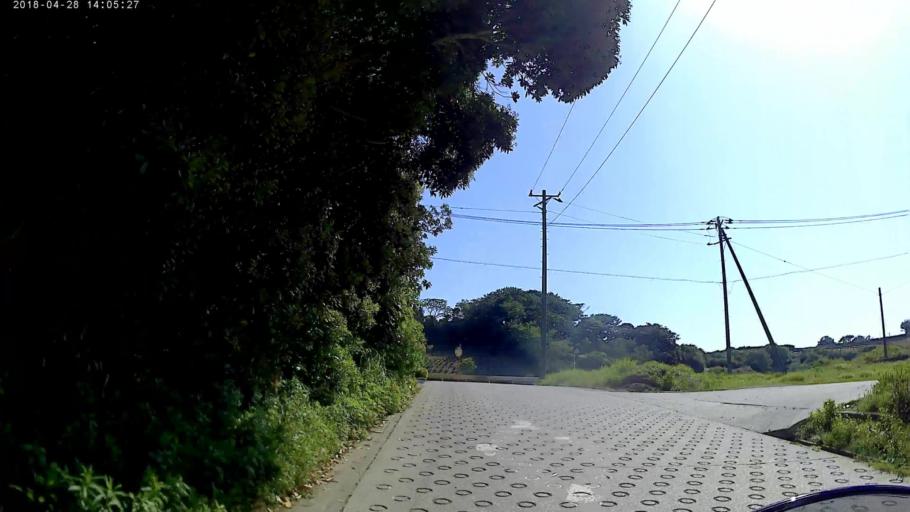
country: JP
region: Kanagawa
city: Miura
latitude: 35.1580
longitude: 139.6510
